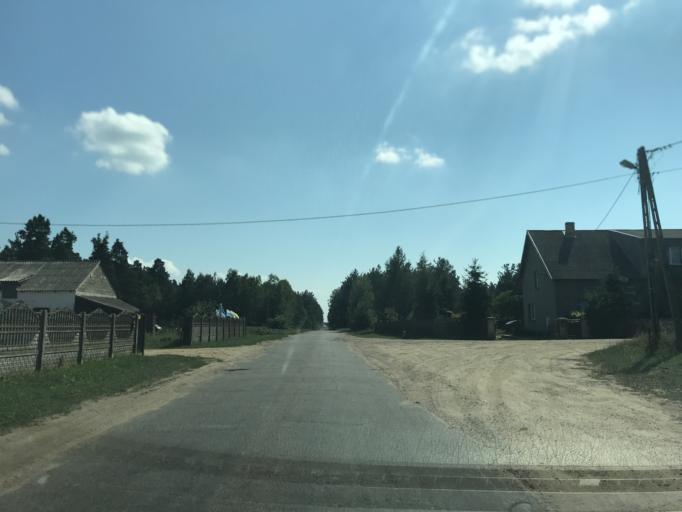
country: PL
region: Masovian Voivodeship
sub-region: Powiat zurominski
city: Zuromin
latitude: 53.1507
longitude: 19.9352
